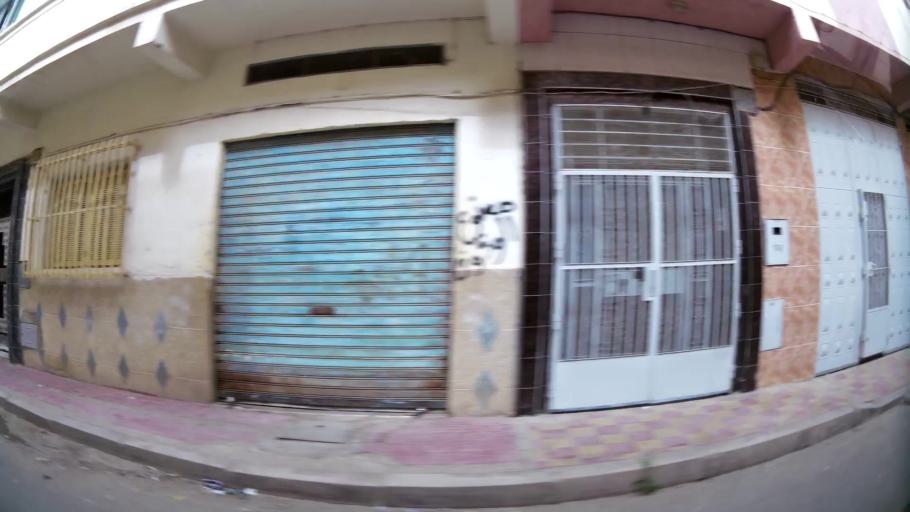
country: MA
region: Oriental
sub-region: Nador
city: Nador
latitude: 35.1650
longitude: -2.9314
